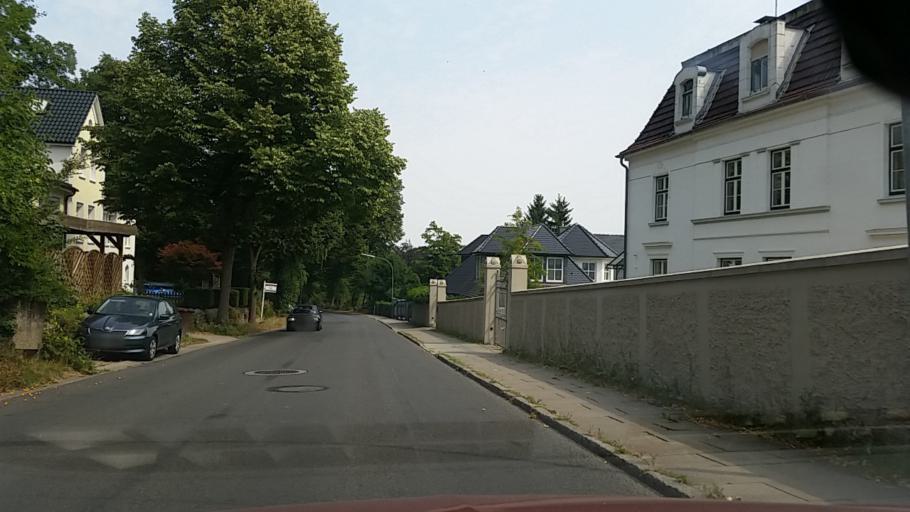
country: DE
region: Schleswig-Holstein
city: Romnitz
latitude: 53.6949
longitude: 10.7582
